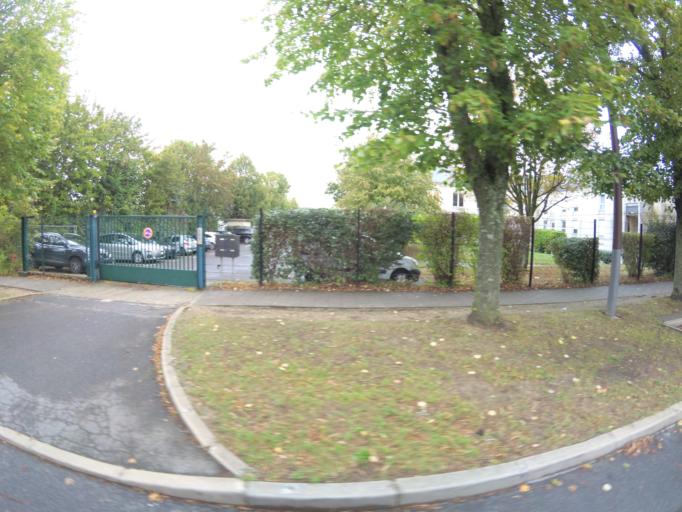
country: FR
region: Ile-de-France
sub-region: Departement de Seine-et-Marne
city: Bussy-Saint-Georges
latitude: 48.8420
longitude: 2.7030
